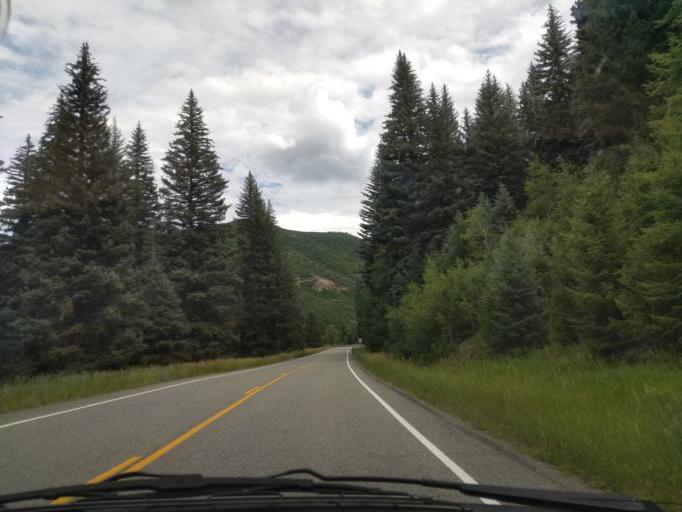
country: US
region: Colorado
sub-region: Delta County
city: Paonia
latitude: 38.9933
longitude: -107.3543
